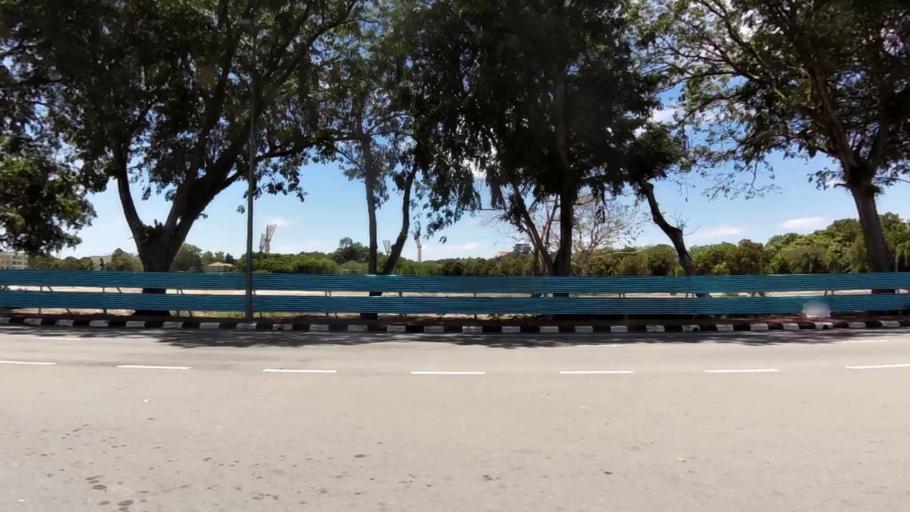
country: BN
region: Brunei and Muara
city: Bandar Seri Begawan
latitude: 4.9302
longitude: 114.9399
